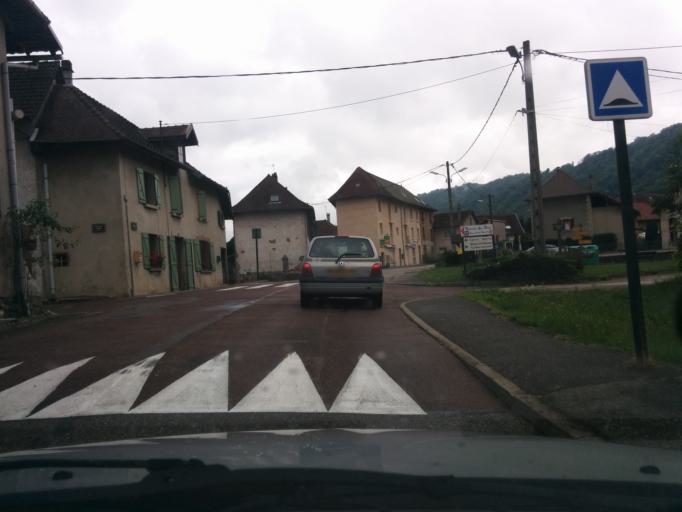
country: FR
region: Rhone-Alpes
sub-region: Departement de l'Isere
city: Saint-Geoire-en-Valdaine
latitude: 45.4760
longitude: 5.6819
